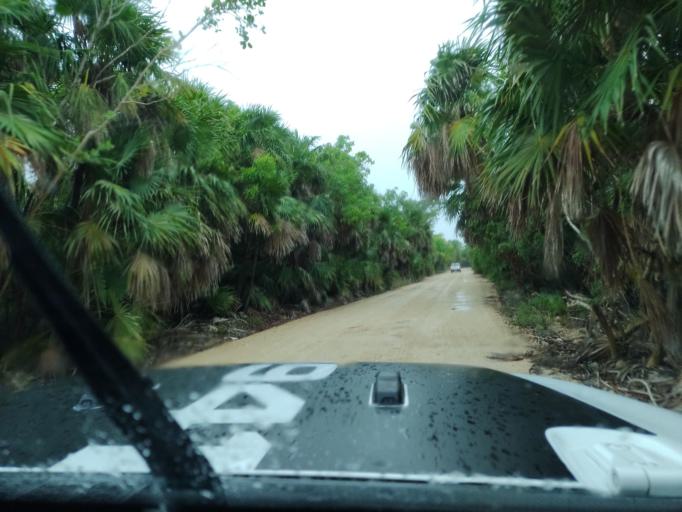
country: MX
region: Quintana Roo
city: Tulum
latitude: 20.0509
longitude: -87.4814
